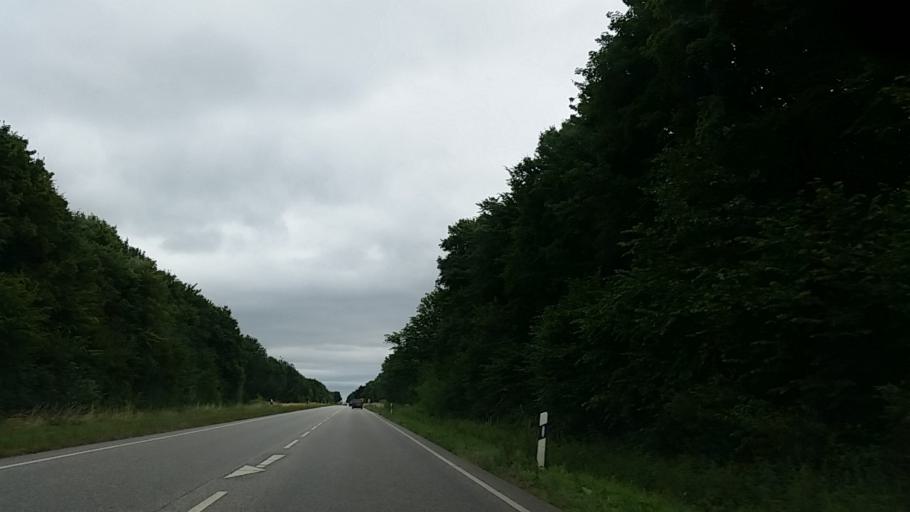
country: DE
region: Schleswig-Holstein
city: Neudorf-Bornstein
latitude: 54.4364
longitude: 9.9328
